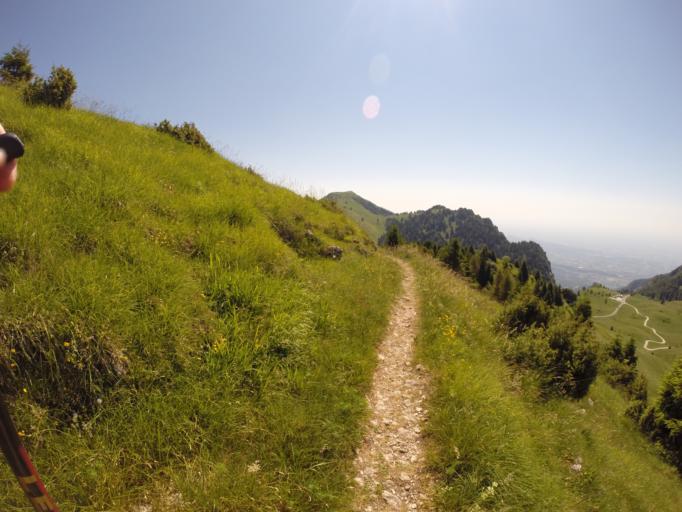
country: IT
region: Veneto
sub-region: Provincia di Treviso
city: Crespano del Grappa
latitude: 45.8867
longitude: 11.8089
